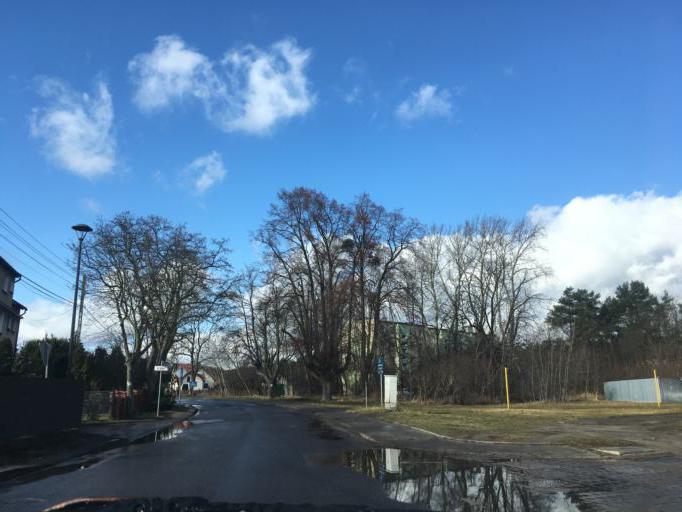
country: PL
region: Pomeranian Voivodeship
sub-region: Powiat gdanski
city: Cedry Wielkie
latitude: 54.3462
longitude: 18.8197
